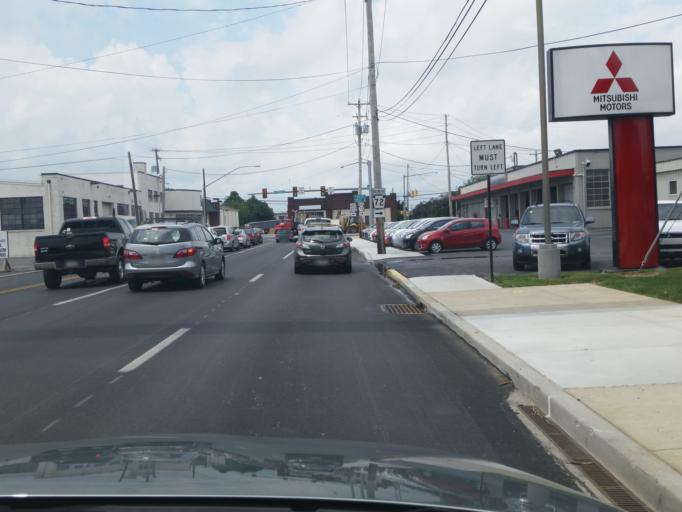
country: US
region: Pennsylvania
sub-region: Lancaster County
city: Lancaster
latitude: 40.0536
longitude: -76.3092
